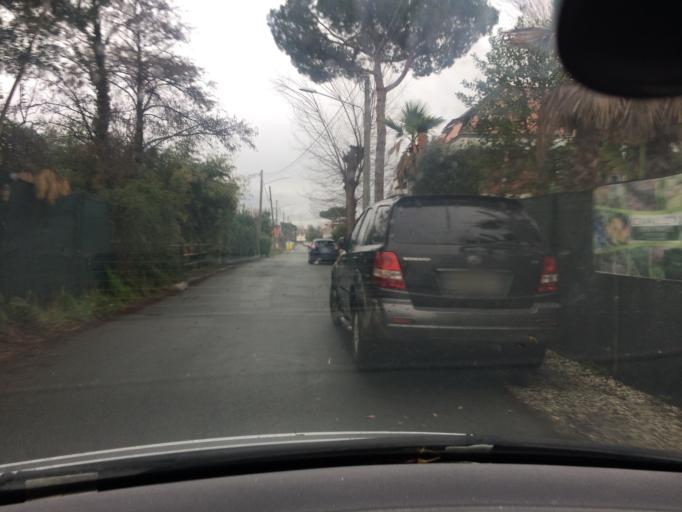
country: IT
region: Tuscany
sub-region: Provincia di Massa-Carrara
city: Massa
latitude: 44.0149
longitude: 10.1015
